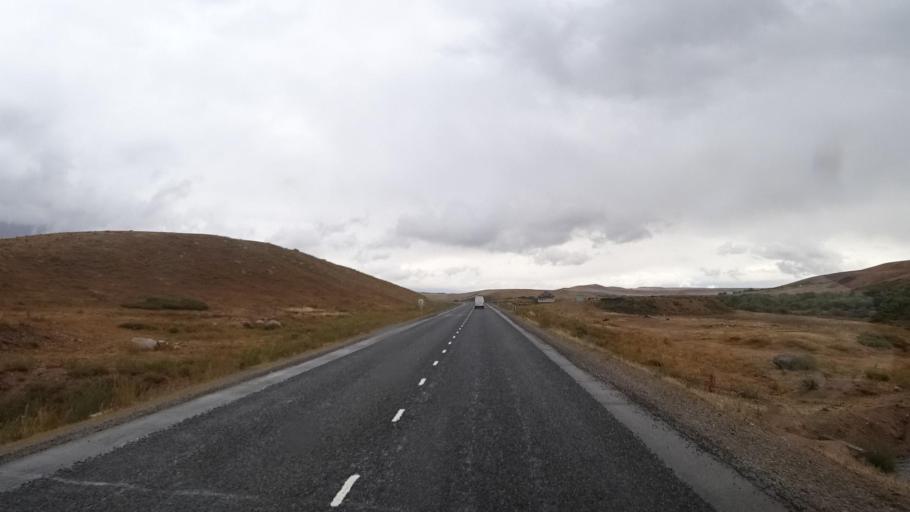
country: KG
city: Sosnovka
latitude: 42.2078
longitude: 73.6643
